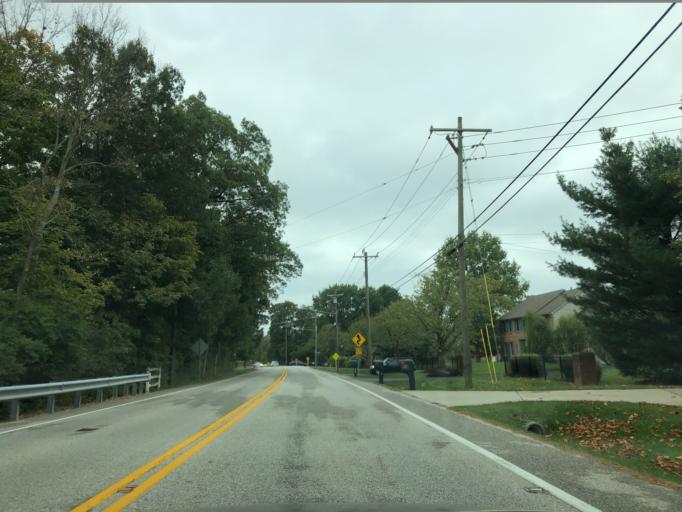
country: US
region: Ohio
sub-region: Hamilton County
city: The Village of Indian Hill
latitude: 39.2613
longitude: -84.3084
